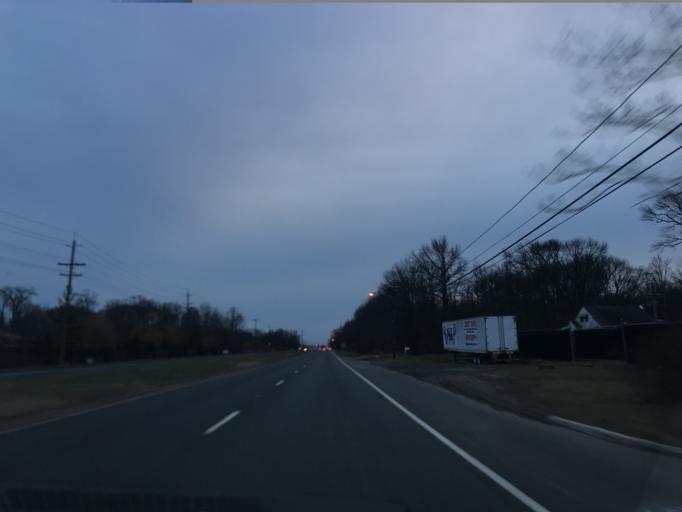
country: US
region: New Jersey
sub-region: Middlesex County
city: Dayton
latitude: 40.3887
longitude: -74.5048
